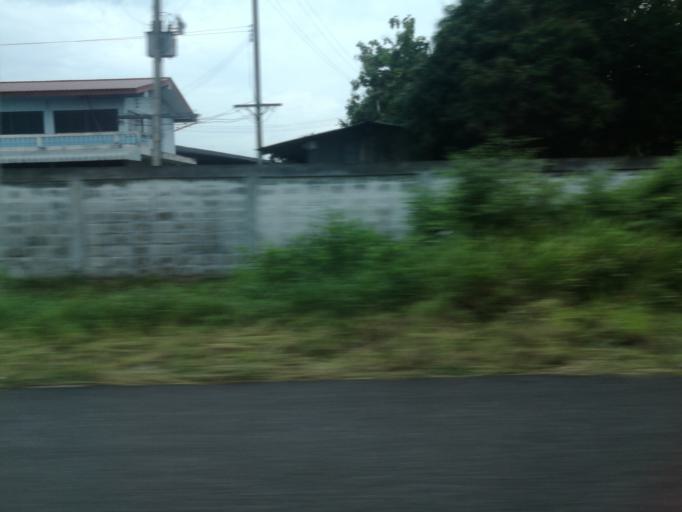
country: TH
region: Prachuap Khiri Khan
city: Kui Buri
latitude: 11.9888
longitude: 99.8313
